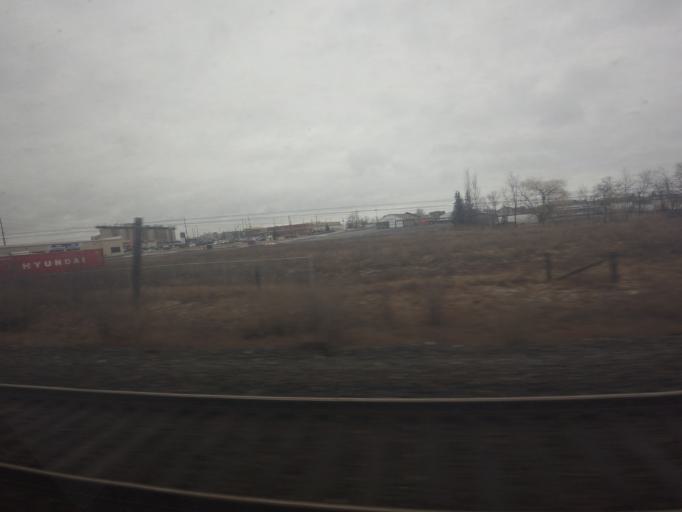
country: CA
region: Ontario
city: Kingston
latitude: 44.2402
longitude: -76.5699
